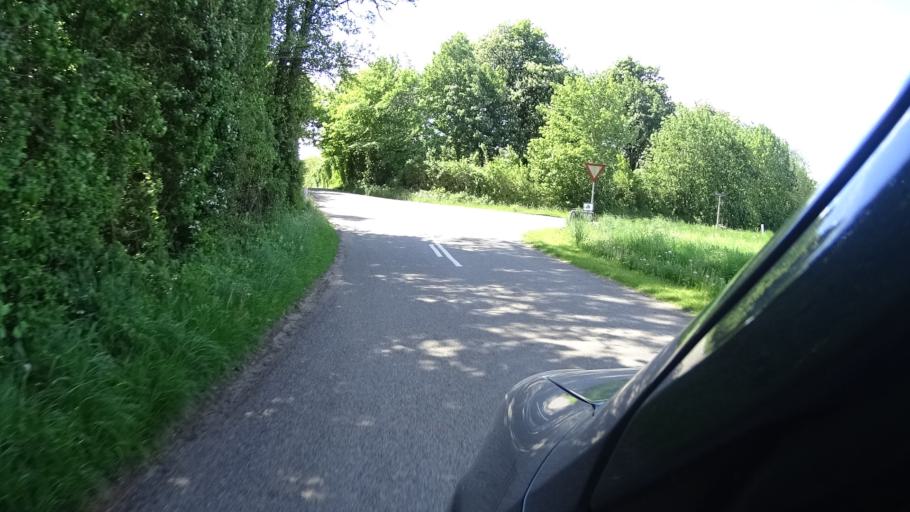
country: DK
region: South Denmark
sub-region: Vejle Kommune
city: Borkop
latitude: 55.6114
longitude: 9.6493
